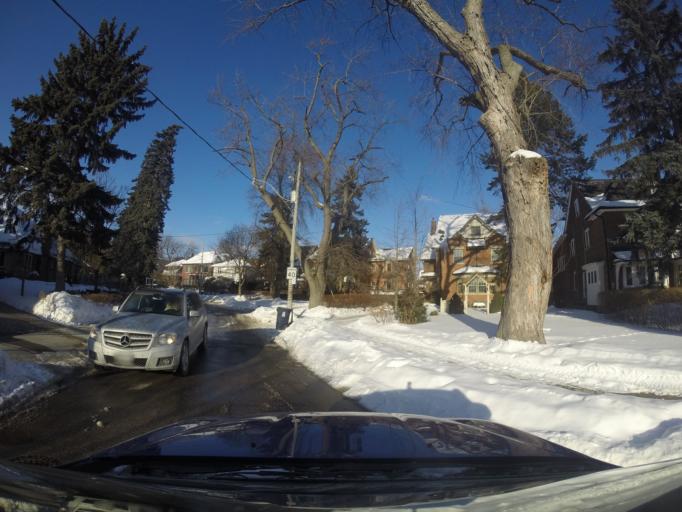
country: CA
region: Ontario
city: Toronto
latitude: 43.7221
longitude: -79.3987
